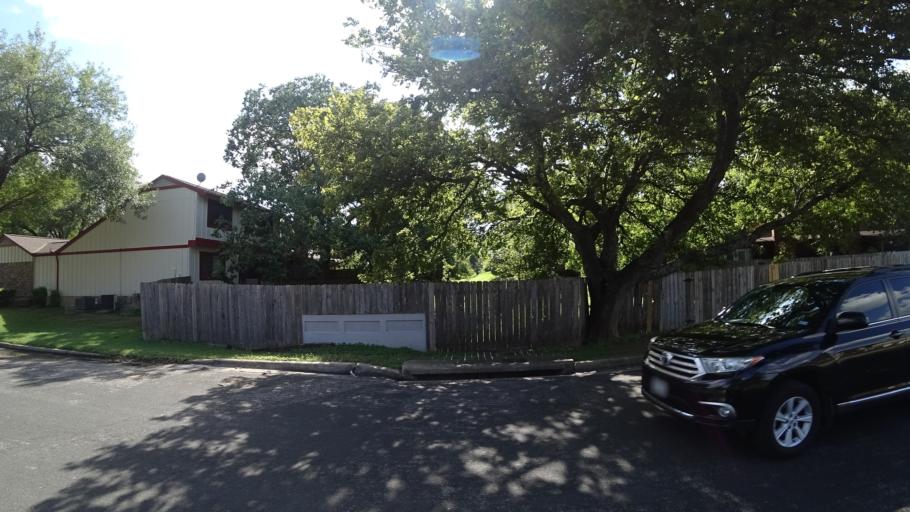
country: US
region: Texas
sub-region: Travis County
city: Wells Branch
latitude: 30.3636
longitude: -97.7088
